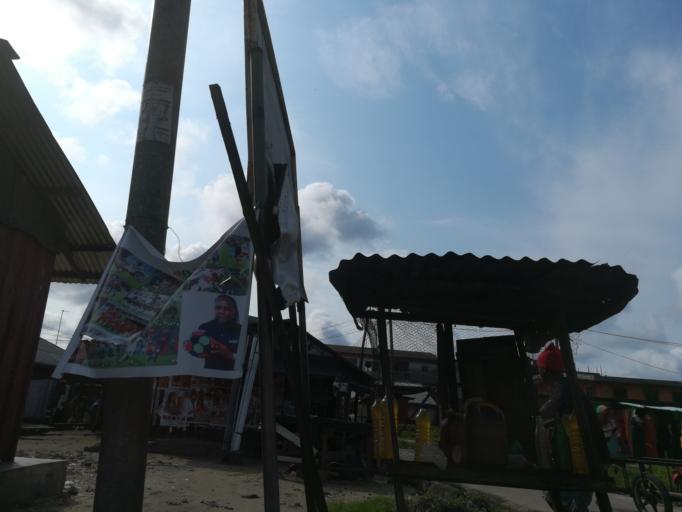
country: NG
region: Rivers
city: Okrika
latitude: 4.7423
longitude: 7.0805
